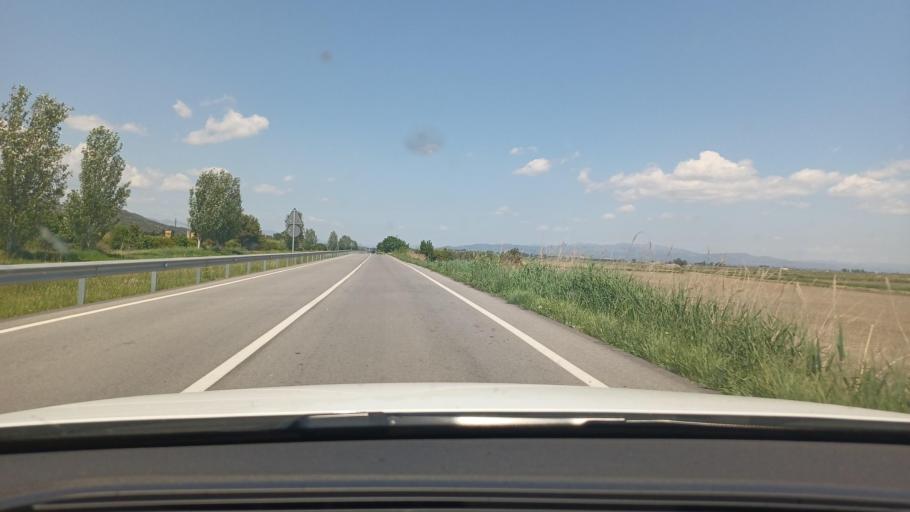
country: ES
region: Catalonia
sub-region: Provincia de Tarragona
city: Sant Carles de la Rapita
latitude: 40.6437
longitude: 0.6000
